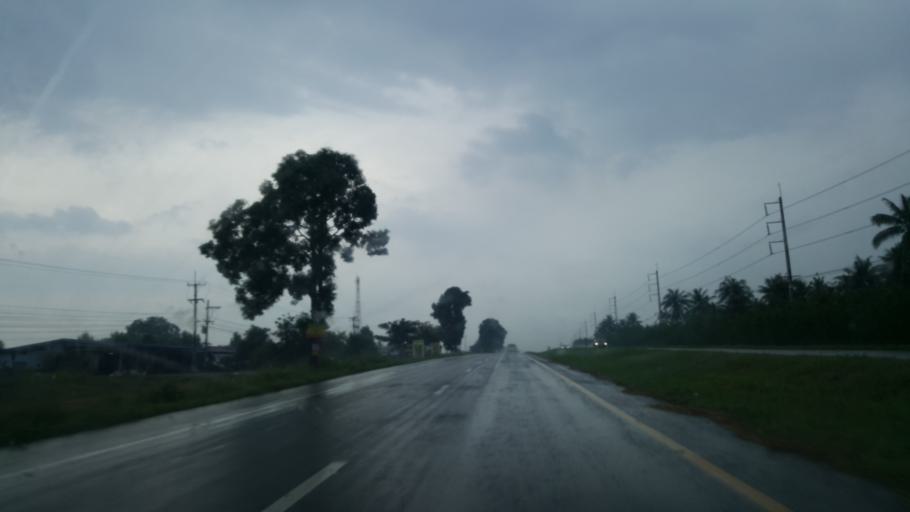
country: TH
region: Chon Buri
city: Ban Talat Bueng
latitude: 12.9641
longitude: 101.0528
